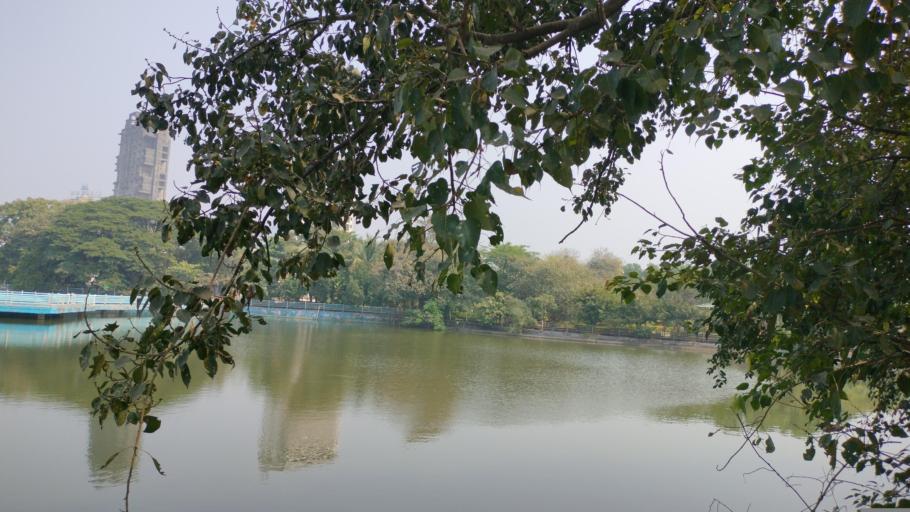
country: IN
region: Maharashtra
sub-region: Thane
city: Navi Mumbai
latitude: 19.0200
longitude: 73.0117
